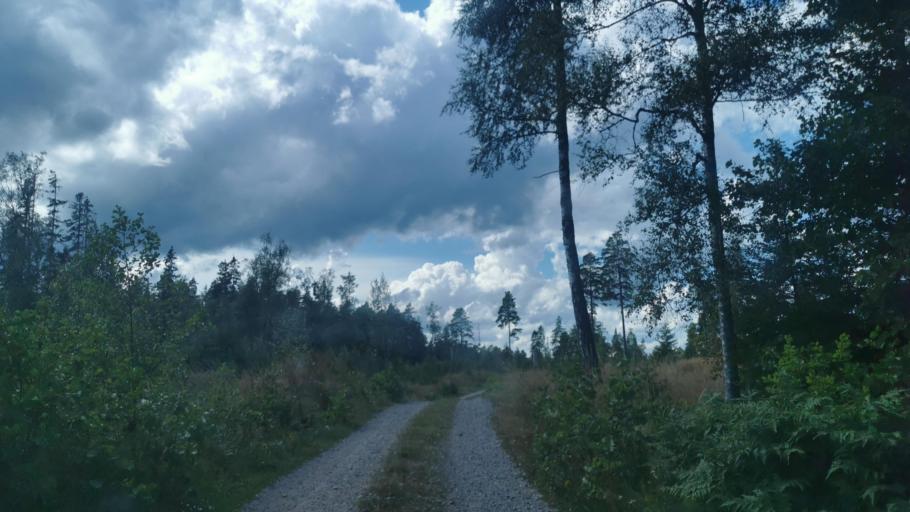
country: SE
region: OEstergoetland
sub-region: Finspangs Kommun
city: Finspang
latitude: 58.7962
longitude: 15.8004
